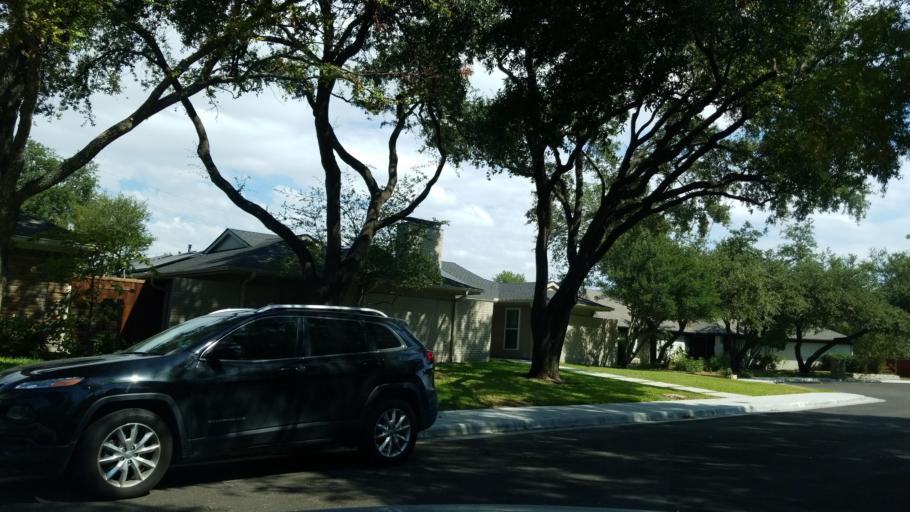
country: US
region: Texas
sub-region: Dallas County
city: Addison
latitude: 32.9618
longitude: -96.7967
